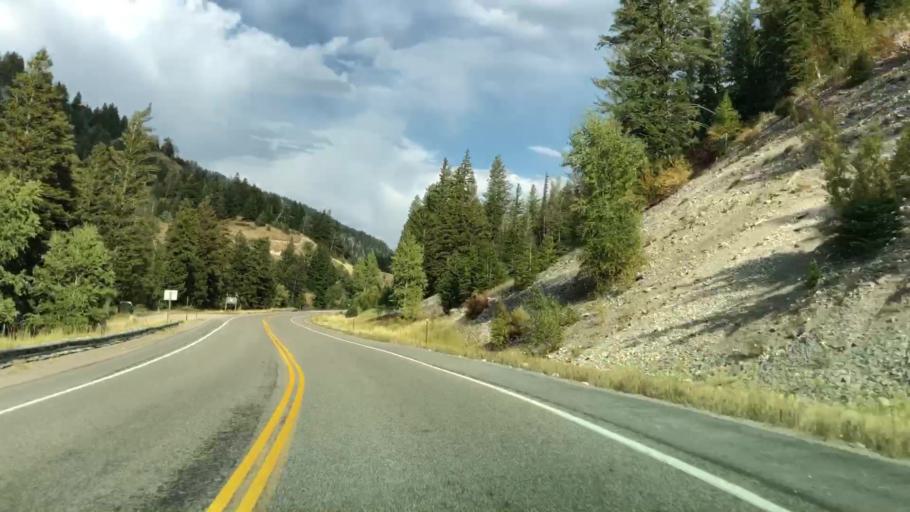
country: US
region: Wyoming
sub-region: Teton County
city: Hoback
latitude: 43.2809
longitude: -110.6159
